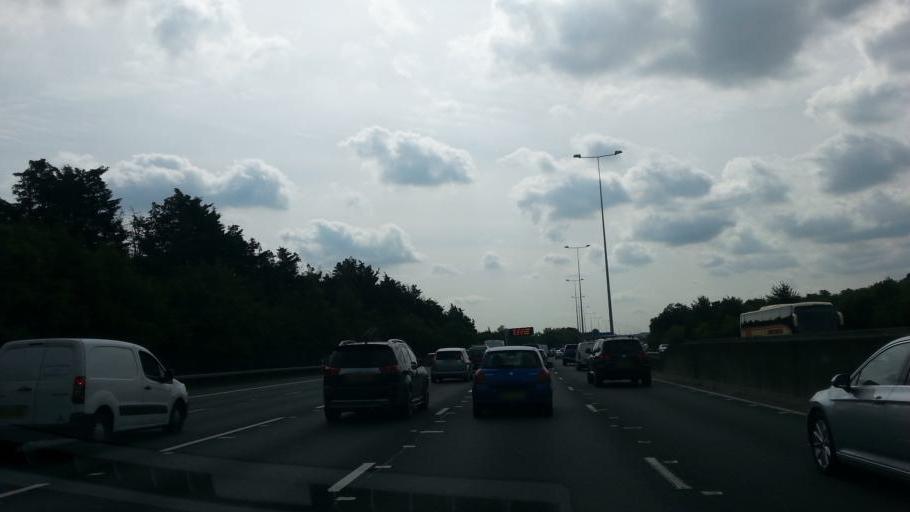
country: GB
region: England
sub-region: Surrey
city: Egham
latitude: 51.4204
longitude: -0.5396
